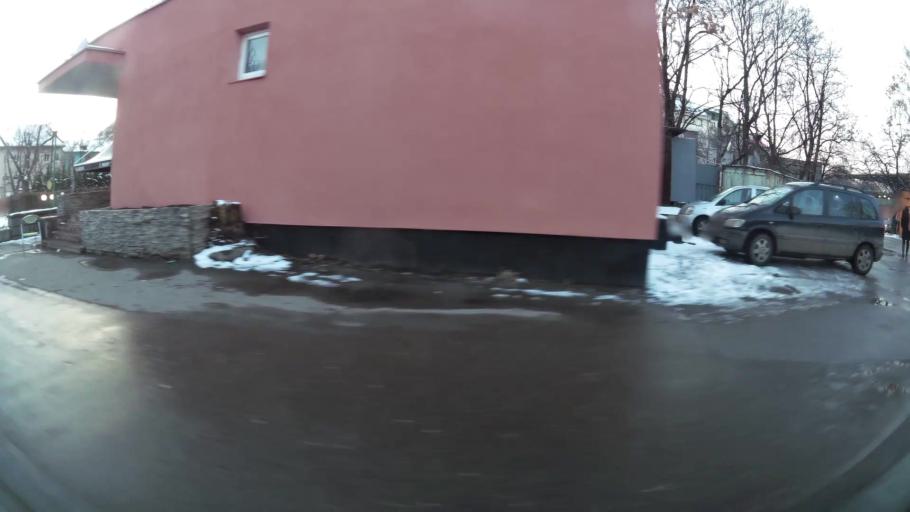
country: BG
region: Sofia-Capital
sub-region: Stolichna Obshtina
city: Sofia
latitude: 42.6809
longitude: 23.3745
